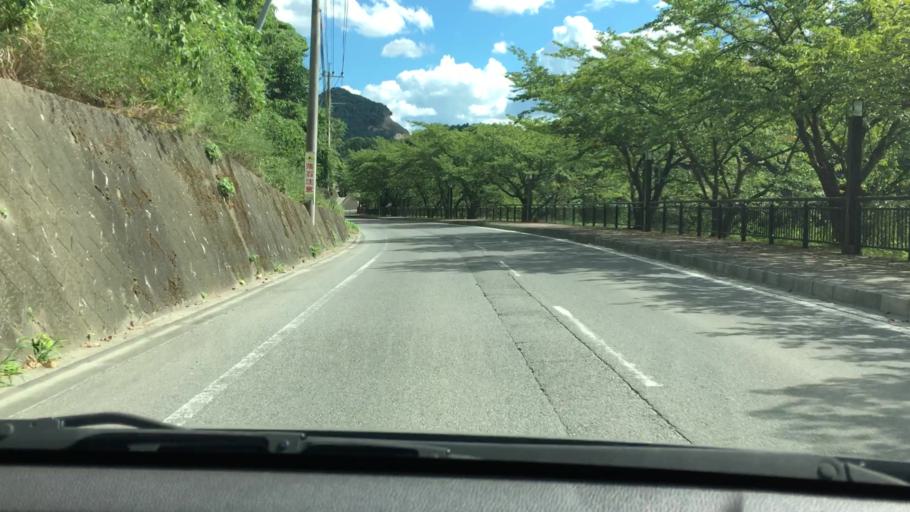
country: JP
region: Saga Prefecture
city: Takeocho-takeo
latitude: 33.1804
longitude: 130.0380
